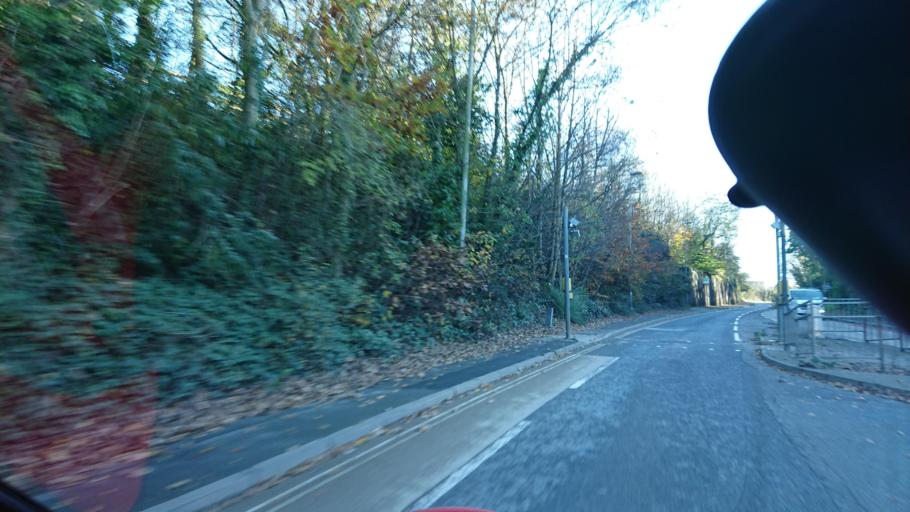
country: GB
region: England
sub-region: Plymouth
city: Plymouth
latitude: 50.4181
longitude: -4.1372
